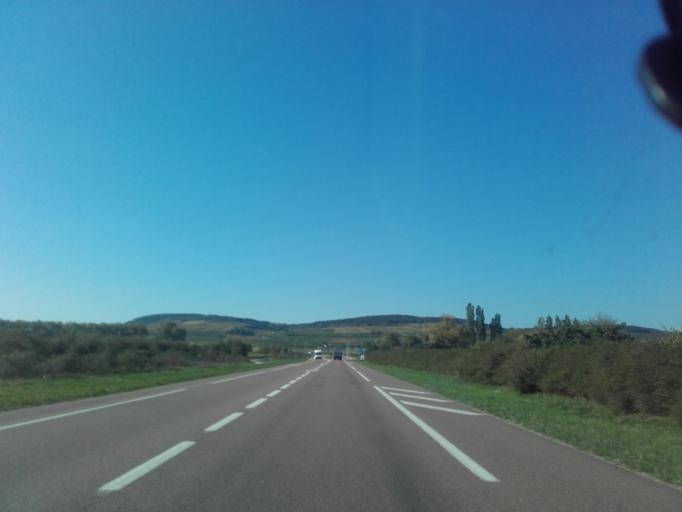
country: FR
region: Bourgogne
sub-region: Departement de la Cote-d'Or
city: Bligny-les-Beaune
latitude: 47.0098
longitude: 4.8190
